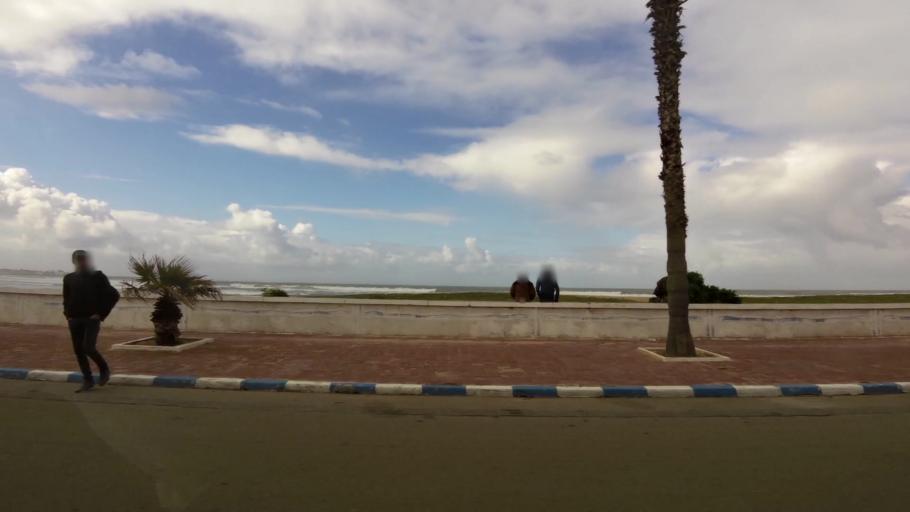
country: MA
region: Doukkala-Abda
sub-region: El-Jadida
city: El Jadida
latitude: 33.2442
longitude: -8.4862
